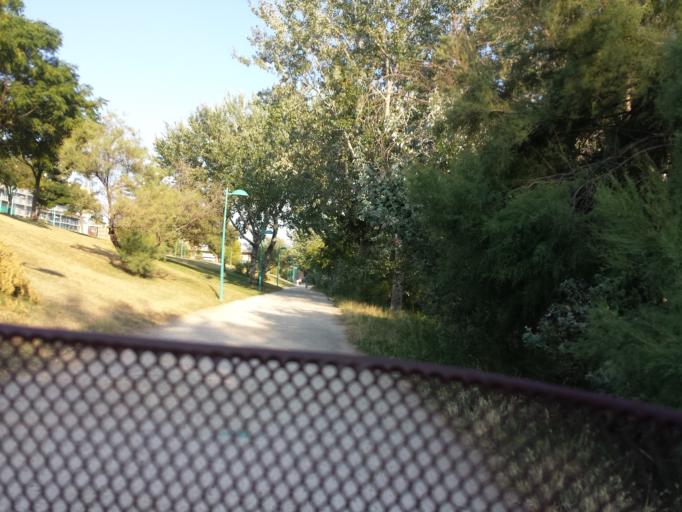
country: ES
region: Aragon
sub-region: Provincia de Zaragoza
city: Zaragoza
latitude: 41.6547
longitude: -0.8658
